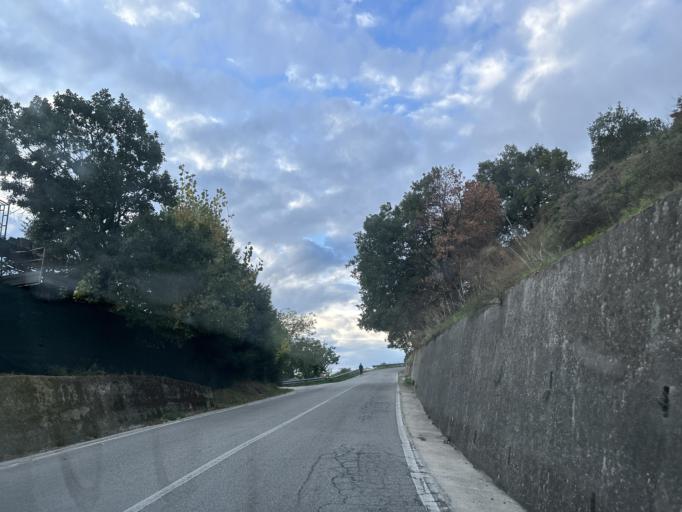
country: IT
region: Calabria
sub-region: Provincia di Catanzaro
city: Montauro
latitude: 38.7467
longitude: 16.5088
